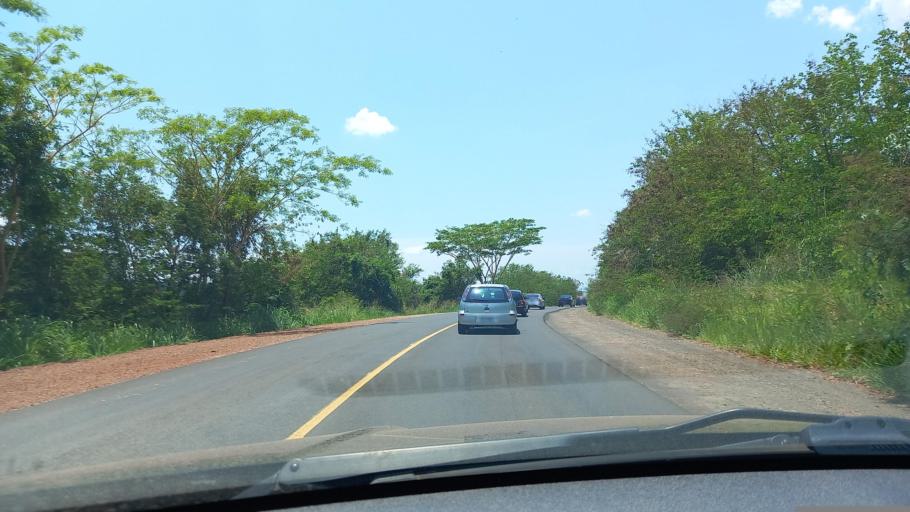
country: BR
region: Sao Paulo
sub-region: Itapira
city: Itapira
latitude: -22.3784
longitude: -46.8691
